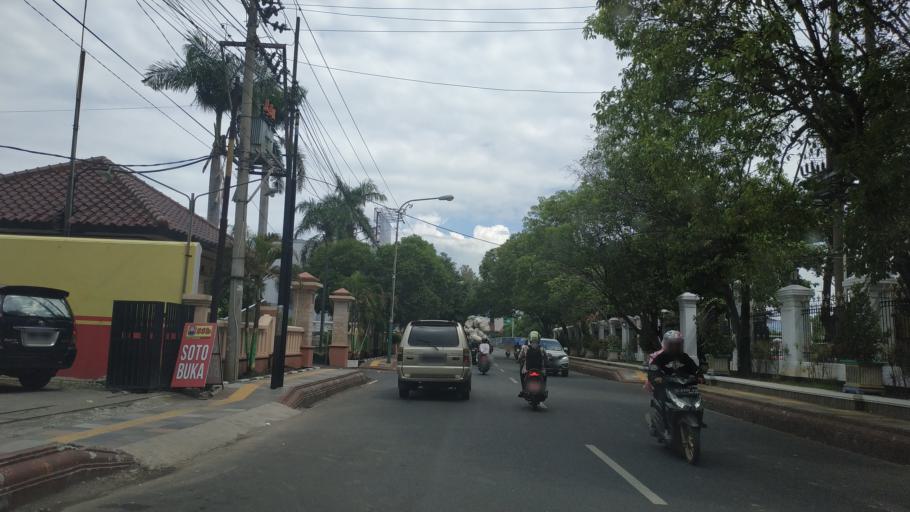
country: ID
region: Central Java
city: Pati
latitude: -6.7521
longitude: 111.0407
